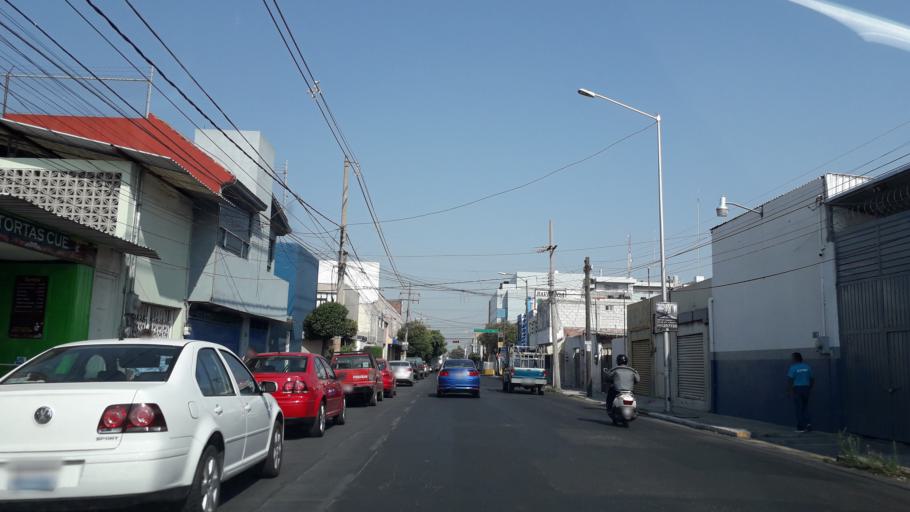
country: MX
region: Puebla
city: Puebla
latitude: 19.0439
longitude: -98.2190
